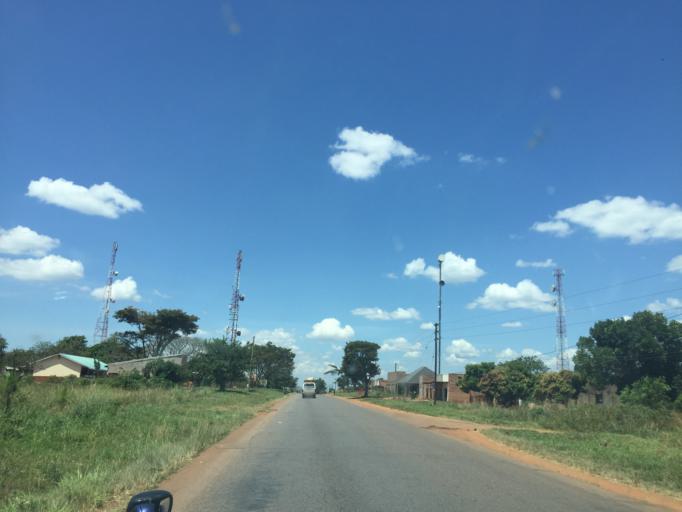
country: UG
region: Western Region
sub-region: Kiryandongo District
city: Masindi Port
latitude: 1.5066
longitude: 32.1012
